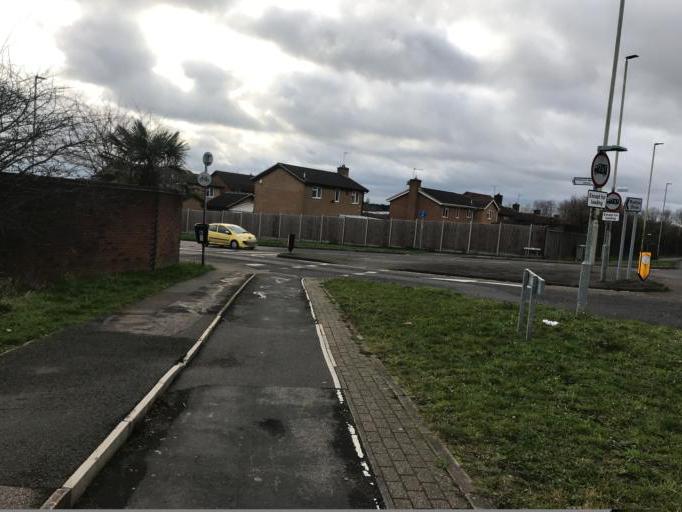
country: GB
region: England
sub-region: Leicestershire
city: Hinckley
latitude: 52.5435
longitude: -1.4010
